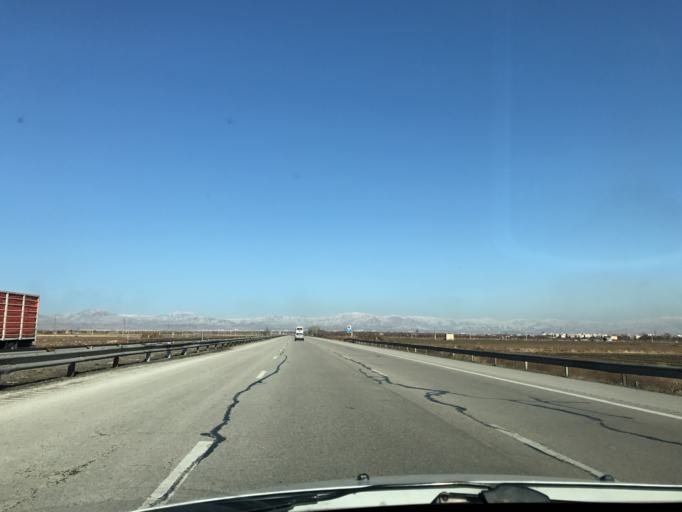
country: IR
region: Qazvin
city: Qazvin
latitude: 36.2270
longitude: 49.8931
